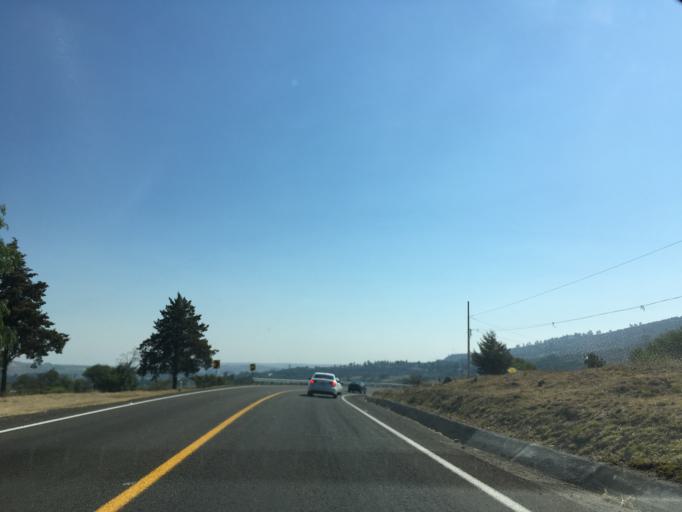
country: MX
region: Michoacan
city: Charo
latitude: 19.7647
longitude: -101.0266
